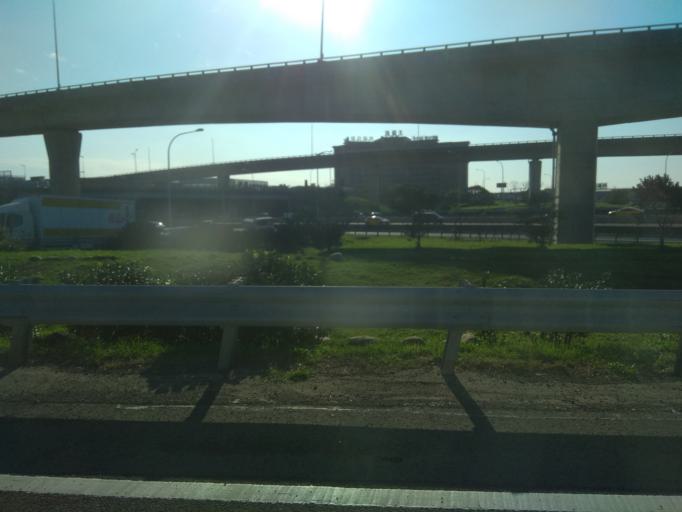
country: TW
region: Taiwan
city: Taoyuan City
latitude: 25.0601
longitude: 121.2140
